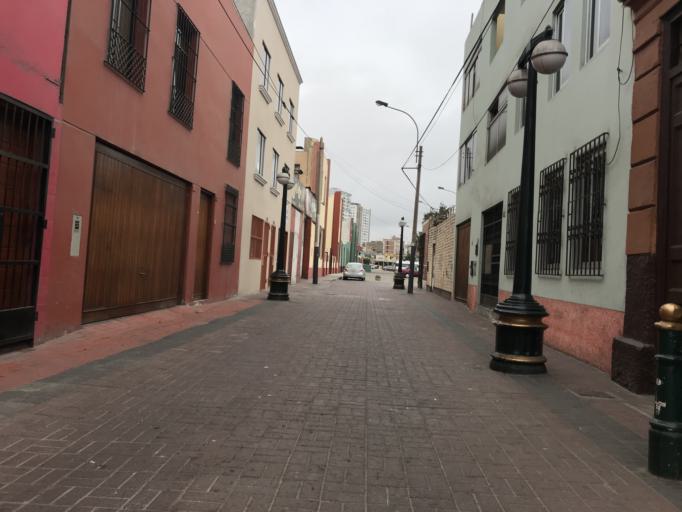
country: PE
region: Lima
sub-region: Lima
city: San Isidro
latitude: -12.0777
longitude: -77.0614
